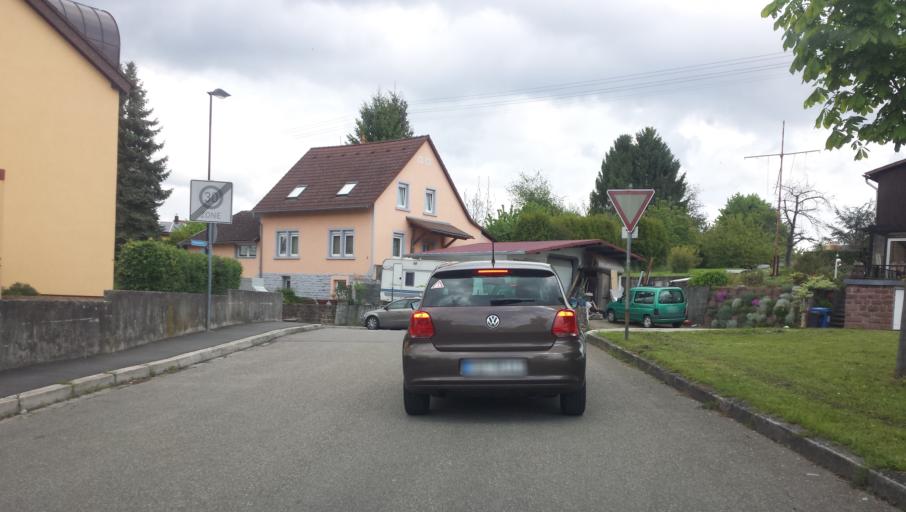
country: DE
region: Baden-Wuerttemberg
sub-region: Karlsruhe Region
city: Obrigheim
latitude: 49.3396
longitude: 9.1046
